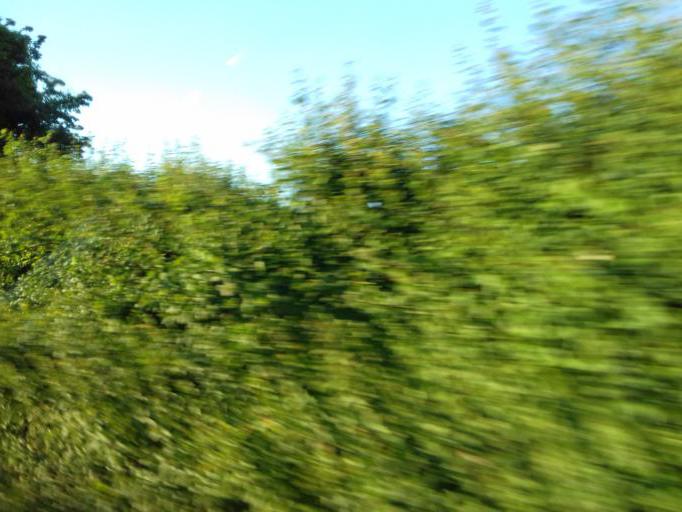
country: IE
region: Leinster
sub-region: An Mhi
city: Ashbourne
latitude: 53.5280
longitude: -6.3606
